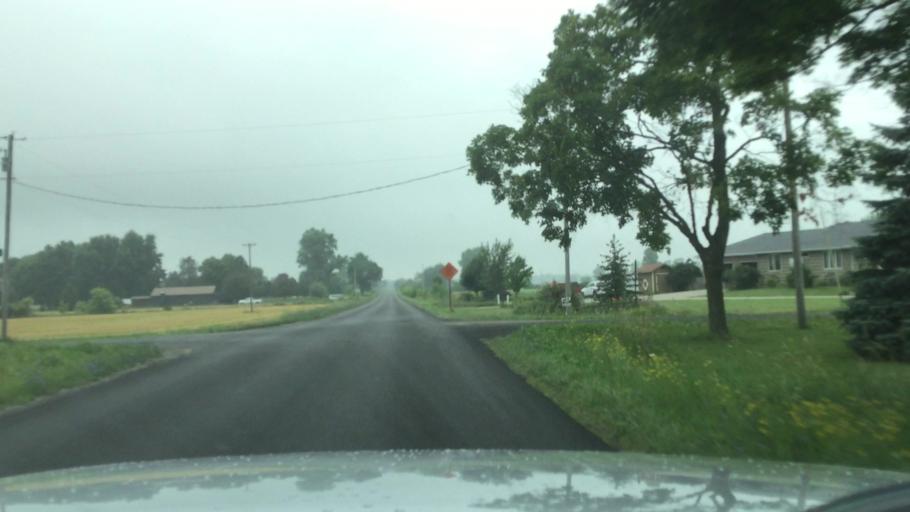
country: US
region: Michigan
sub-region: Shiawassee County
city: New Haven
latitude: 43.0573
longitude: -84.1481
